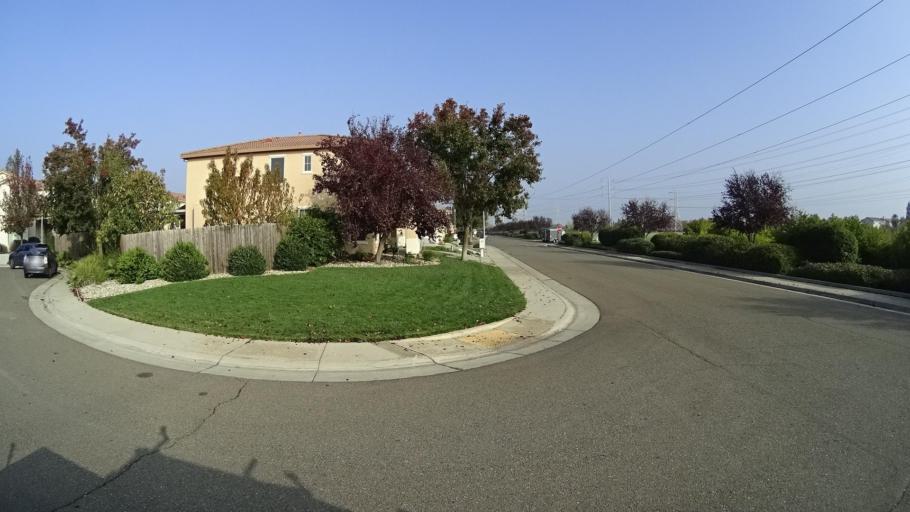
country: US
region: California
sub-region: Sacramento County
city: Elk Grove
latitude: 38.4046
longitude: -121.3512
